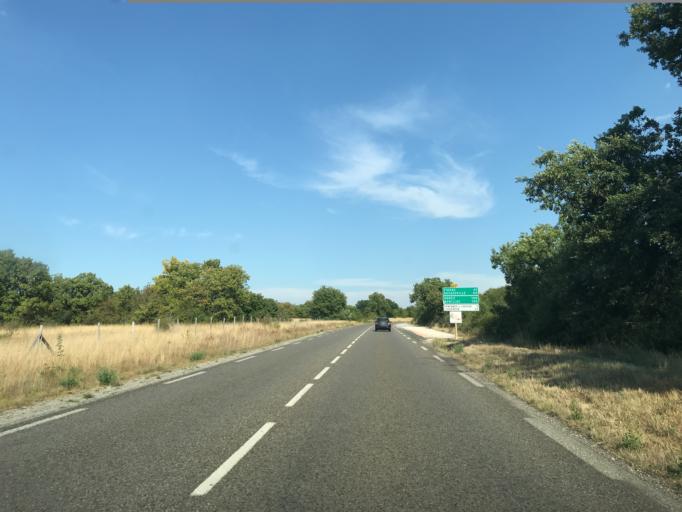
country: FR
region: Midi-Pyrenees
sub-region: Departement du Lot
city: Gramat
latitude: 44.6854
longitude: 1.6084
